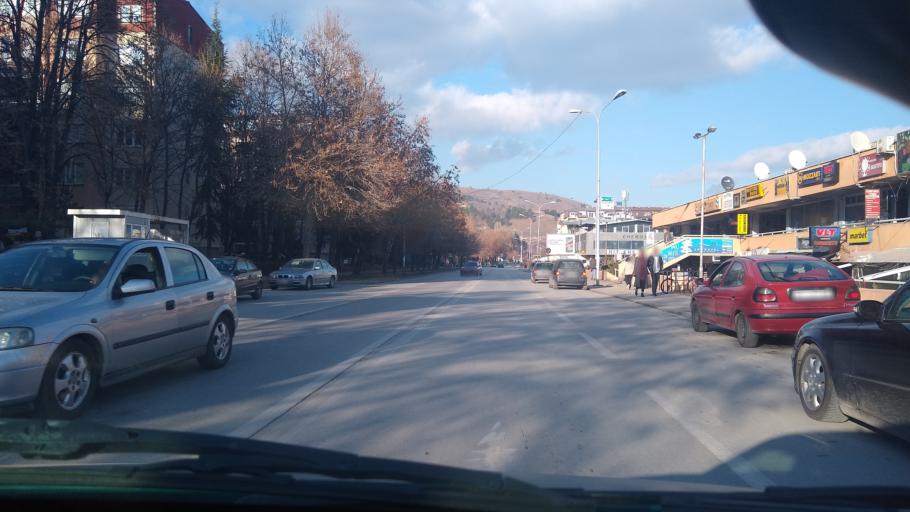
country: MK
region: Bitola
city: Bitola
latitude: 41.0272
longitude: 21.3136
